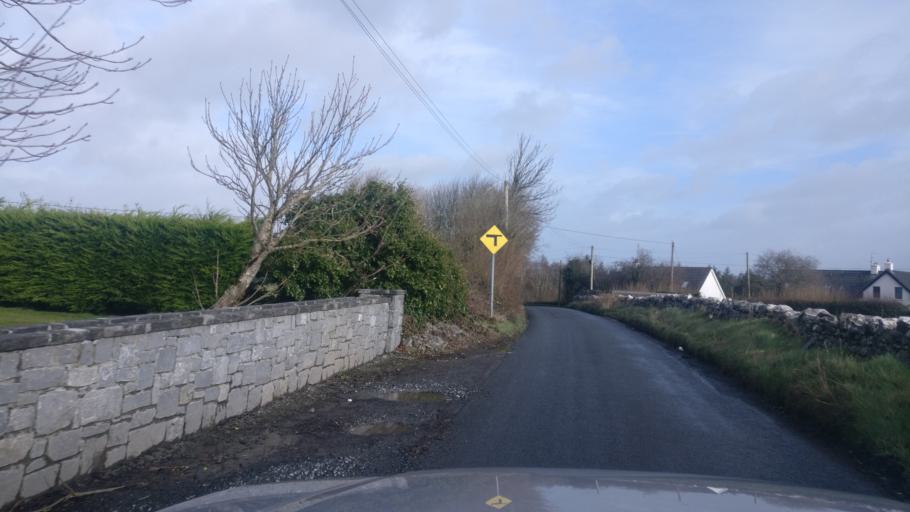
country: IE
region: Connaught
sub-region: County Galway
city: Loughrea
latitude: 53.2777
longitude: -8.5827
